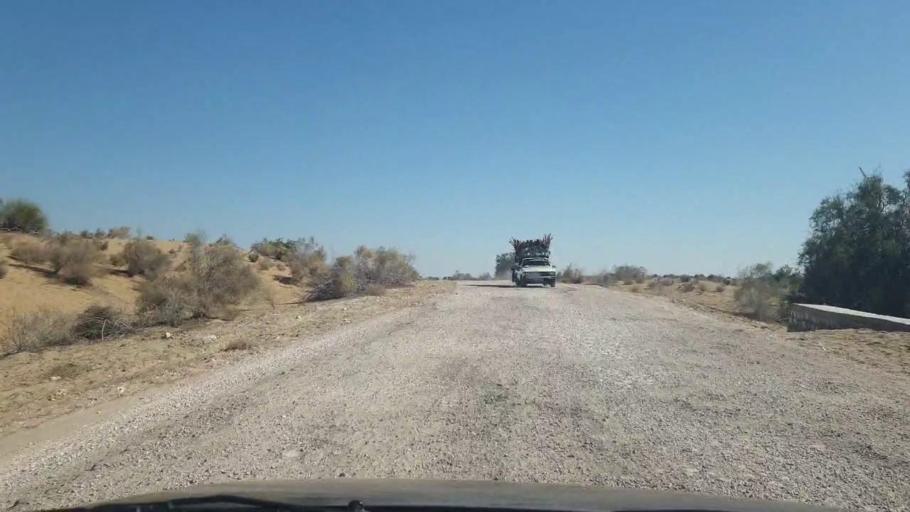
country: PK
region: Sindh
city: Bozdar
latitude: 27.0033
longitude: 68.8837
